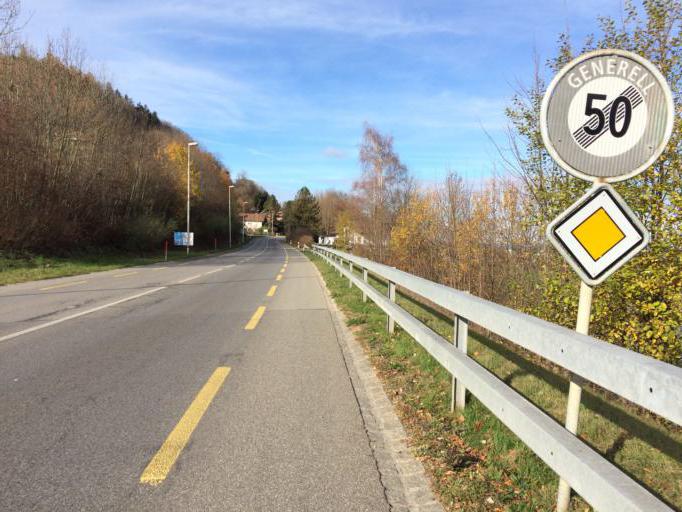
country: CH
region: Bern
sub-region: Bern-Mittelland District
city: Kehrsatz
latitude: 46.9017
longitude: 7.4850
